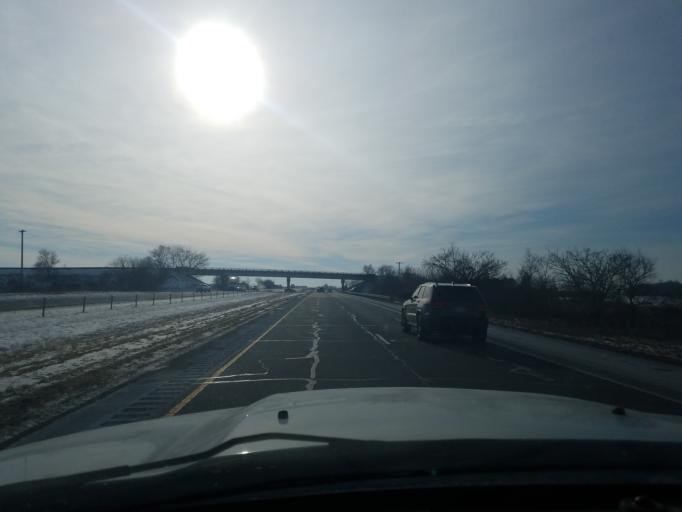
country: US
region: Indiana
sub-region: Huntington County
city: Warren
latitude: 40.6982
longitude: -85.4647
